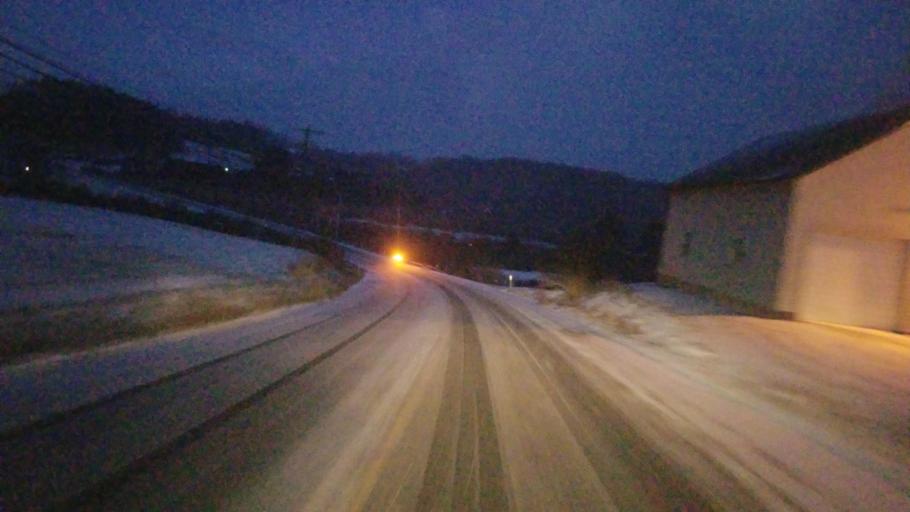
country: US
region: Pennsylvania
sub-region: Clarion County
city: Knox
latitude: 41.2308
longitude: -79.5826
